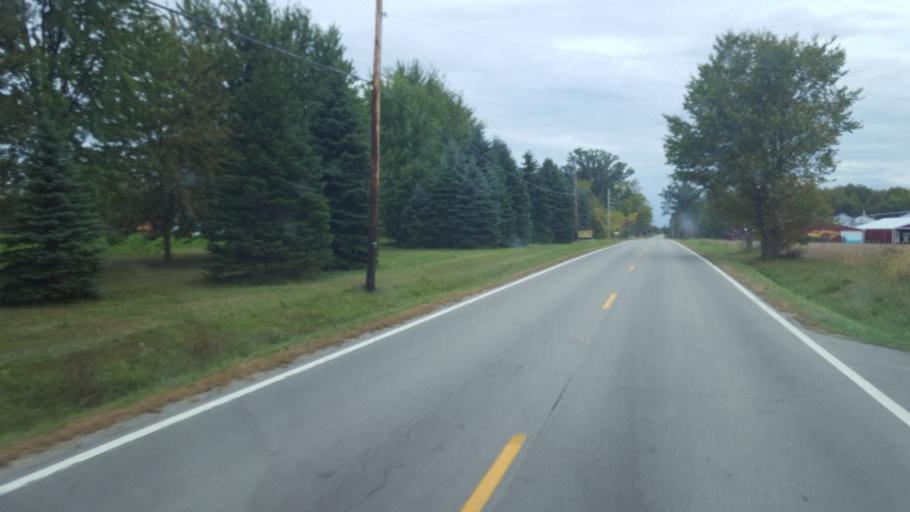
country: US
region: Ohio
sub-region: Huron County
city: Wakeman
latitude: 41.2876
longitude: -82.3787
